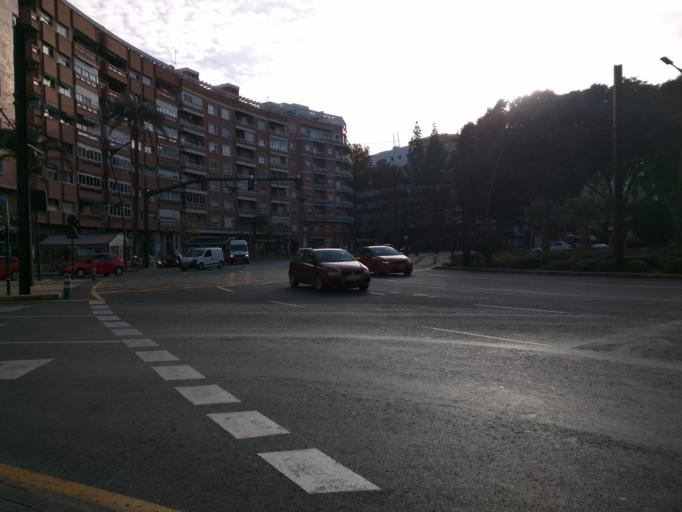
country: ES
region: Murcia
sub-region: Murcia
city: Murcia
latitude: 37.9925
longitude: -1.1295
